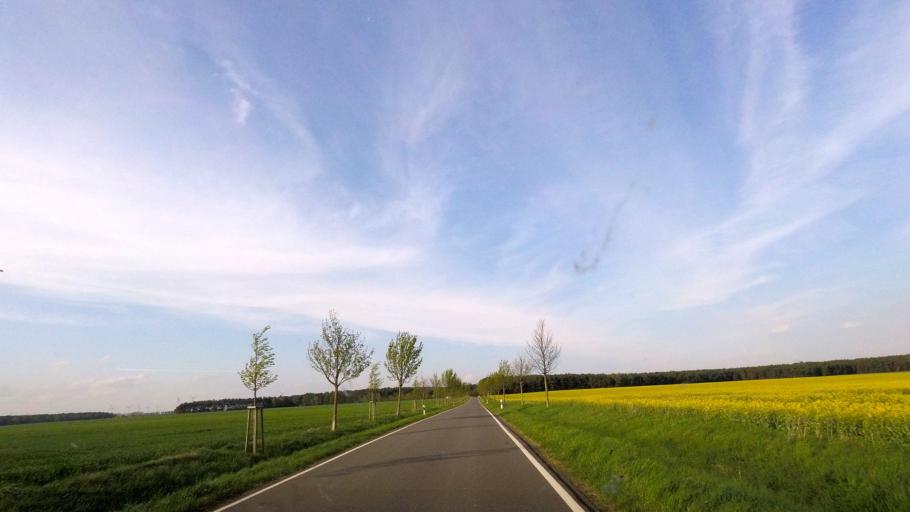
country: DE
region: Saxony-Anhalt
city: Zahna
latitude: 51.9549
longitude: 12.8459
